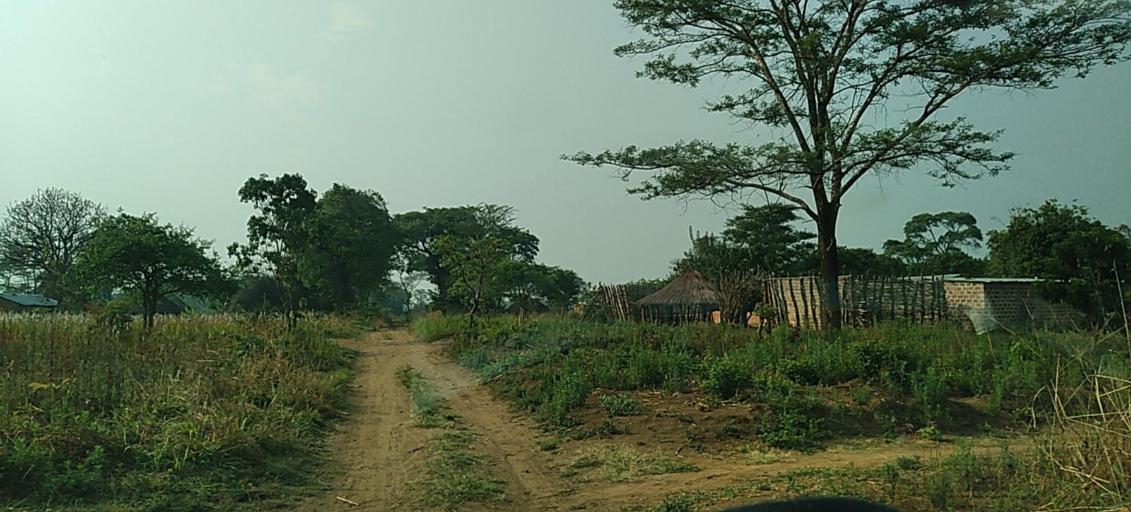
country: ZM
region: North-Western
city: Solwezi
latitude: -12.3722
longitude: 26.5598
